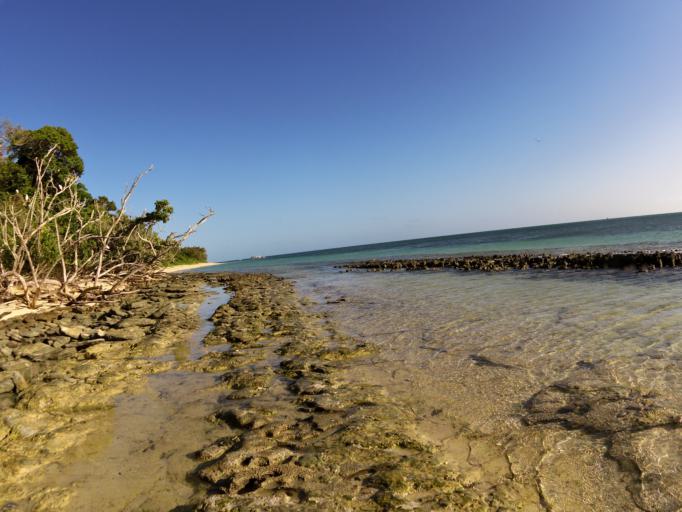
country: AU
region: Queensland
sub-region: Cairns
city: Yorkeys Knob
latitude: -16.7595
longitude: 145.9764
